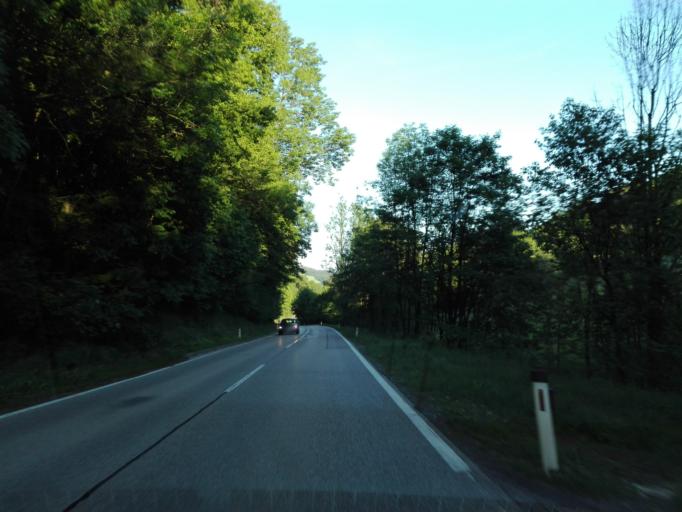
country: AT
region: Upper Austria
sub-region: Politischer Bezirk Rohrbach
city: Kleinzell im Muehlkreis
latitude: 48.3972
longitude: 13.9189
